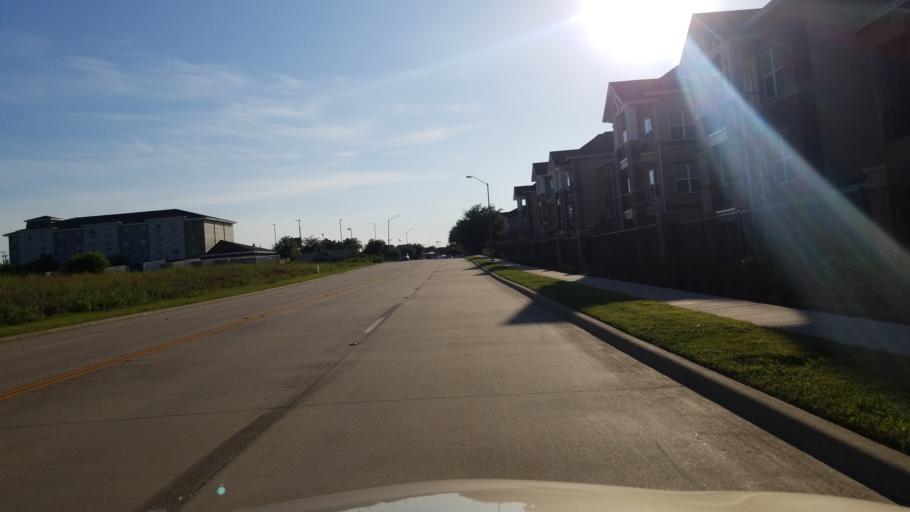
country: US
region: Texas
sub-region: Dallas County
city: Grand Prairie
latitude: 32.6777
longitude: -97.0377
